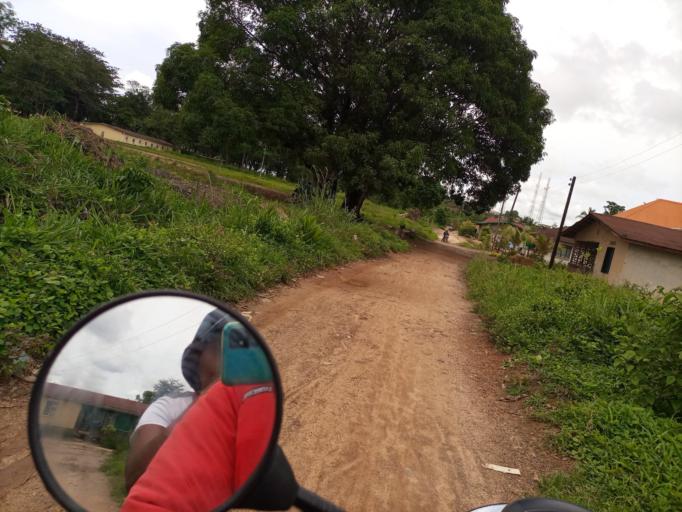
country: SL
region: Southern Province
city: Bo
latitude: 7.9530
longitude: -11.7453
